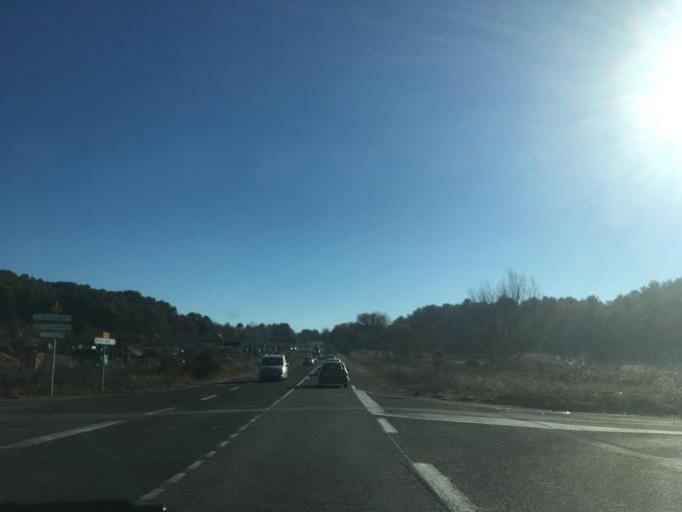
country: FR
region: Provence-Alpes-Cote d'Azur
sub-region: Departement du Var
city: Flayosc
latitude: 43.5337
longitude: 6.4100
